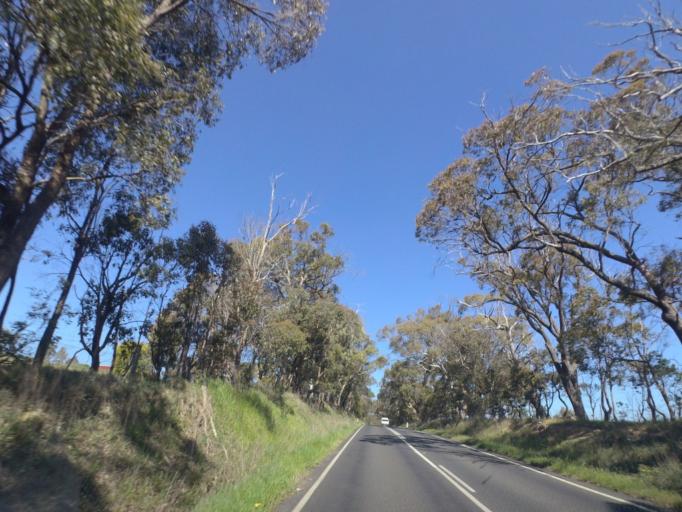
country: AU
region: Victoria
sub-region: Whittlesea
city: Whittlesea
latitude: -37.3436
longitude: 144.9954
